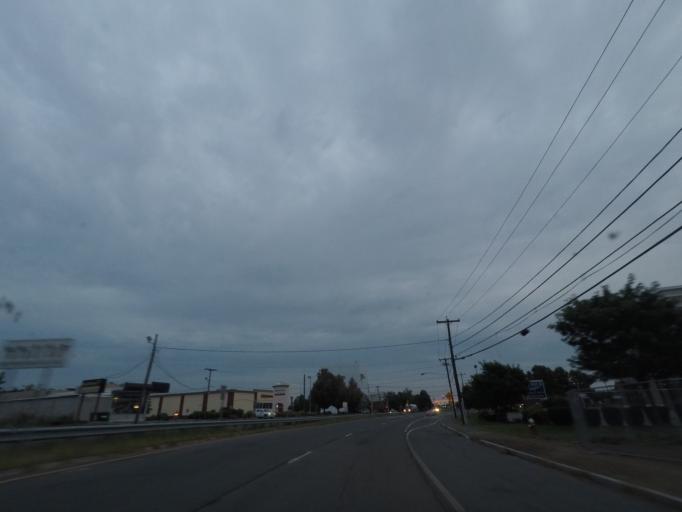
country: US
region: Massachusetts
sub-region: Hampden County
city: West Springfield
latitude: 42.1281
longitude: -72.6266
